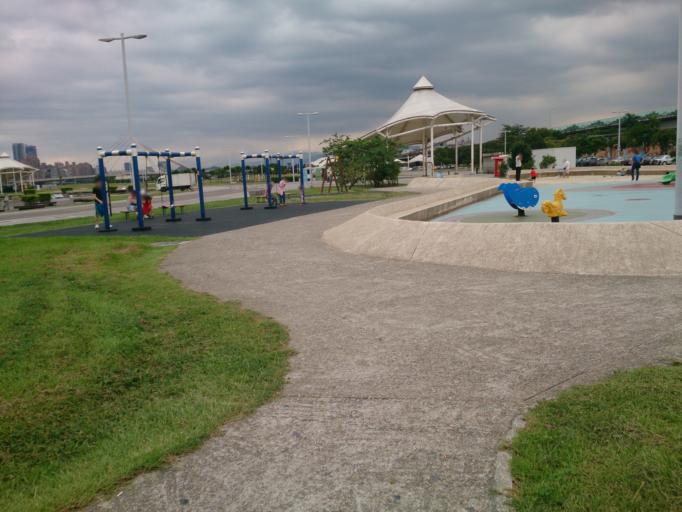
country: TW
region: Taipei
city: Taipei
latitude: 25.0748
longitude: 121.5347
